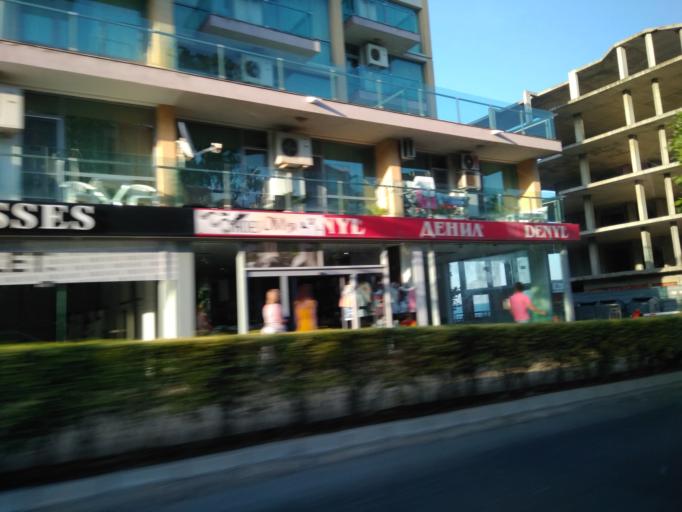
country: BG
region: Burgas
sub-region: Obshtina Nesebur
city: Nesebar
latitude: 42.6613
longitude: 27.7222
